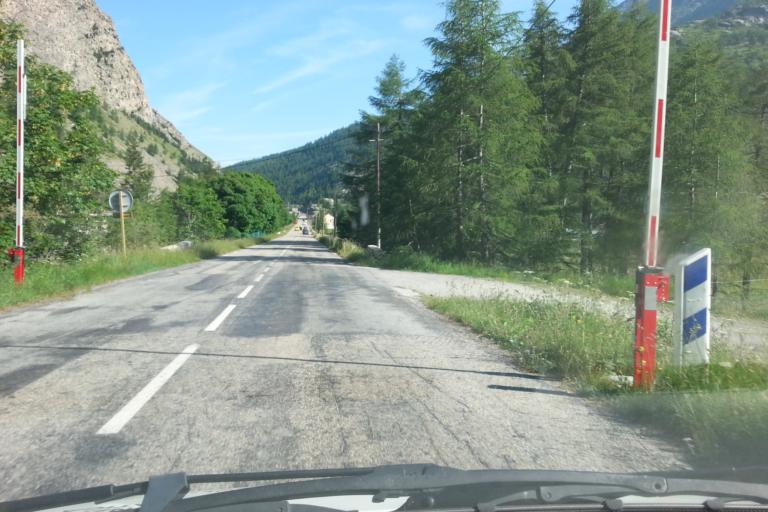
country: IT
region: Piedmont
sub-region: Provincia di Torino
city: Moncenisio
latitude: 45.2145
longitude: 6.9559
